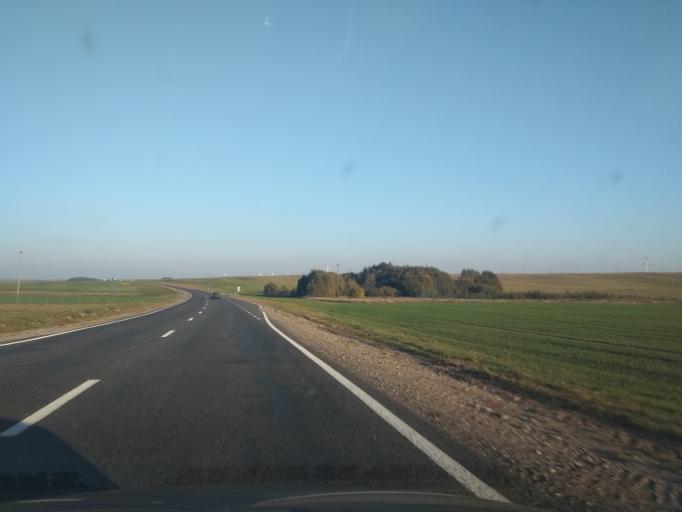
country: BY
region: Grodnenskaya
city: Zel'va
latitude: 53.1375
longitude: 24.7244
